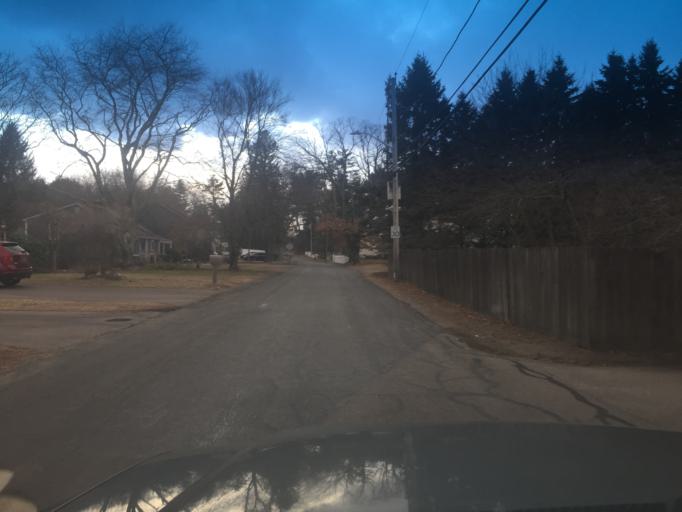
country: US
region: Massachusetts
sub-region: Norfolk County
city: Medway
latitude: 42.1243
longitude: -71.4363
